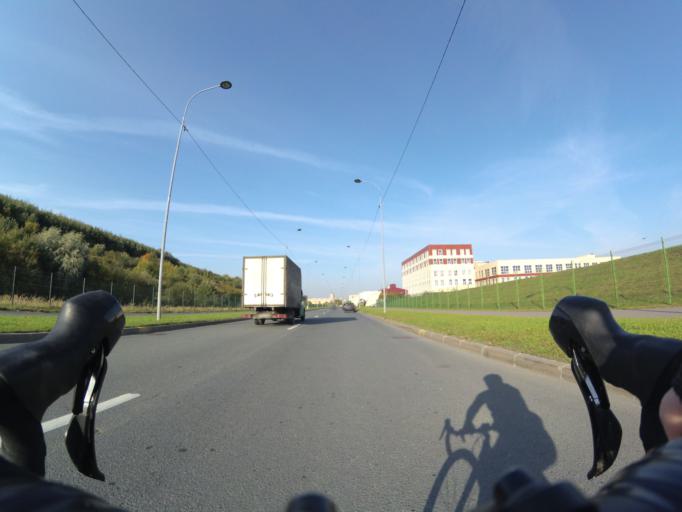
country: RU
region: St.-Petersburg
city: Staraya Derevnya
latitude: 59.9953
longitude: 30.2255
